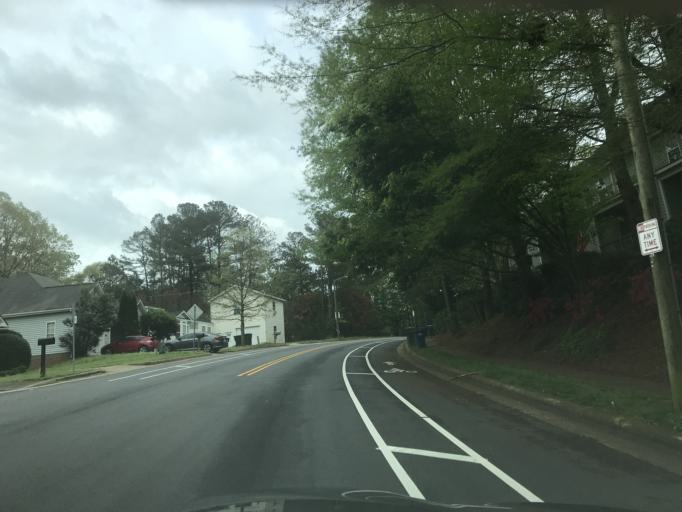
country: US
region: North Carolina
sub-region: Wake County
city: West Raleigh
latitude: 35.7510
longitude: -78.6794
